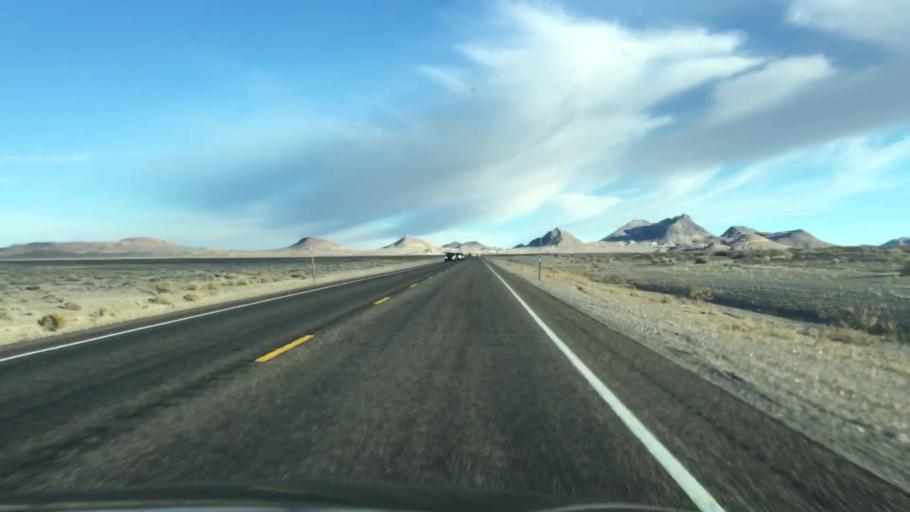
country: US
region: Nevada
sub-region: Nye County
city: Tonopah
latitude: 38.0964
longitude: -117.3172
